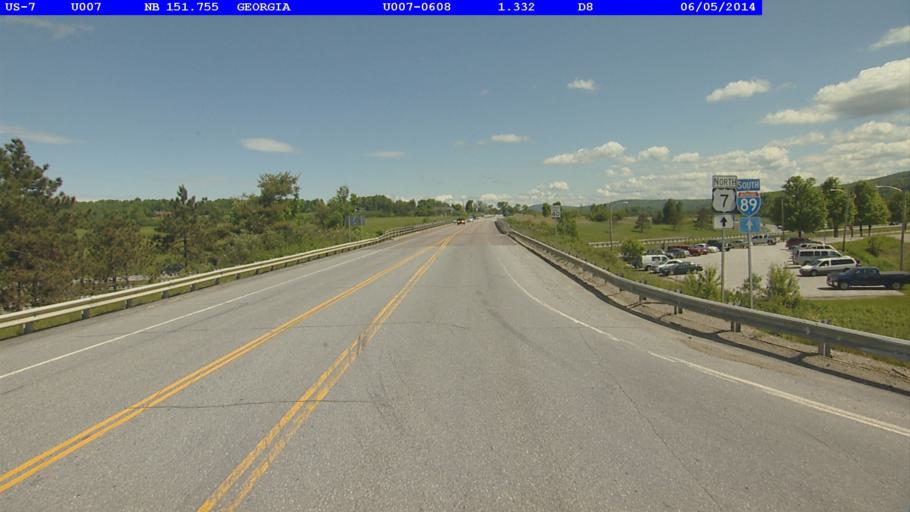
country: US
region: Vermont
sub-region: Chittenden County
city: Milton
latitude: 44.6981
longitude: -73.1067
